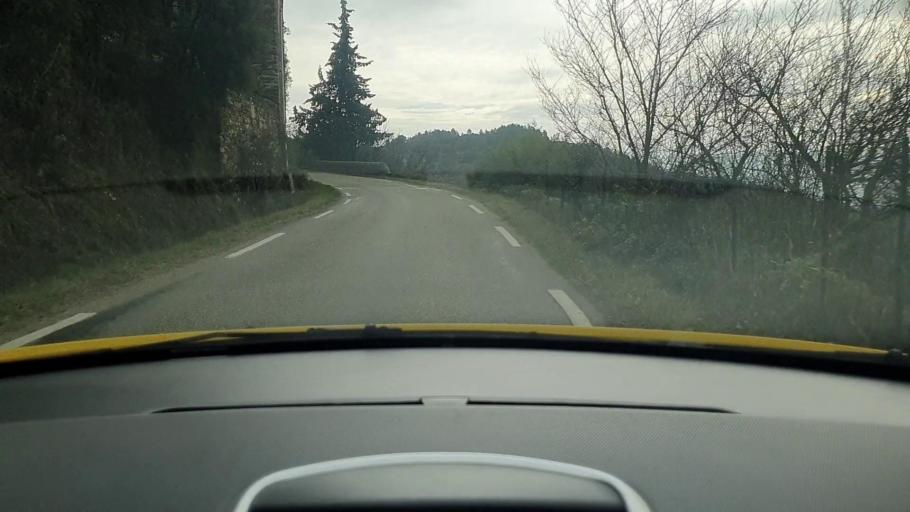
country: FR
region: Languedoc-Roussillon
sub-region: Departement du Gard
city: Besseges
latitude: 44.3391
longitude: 4.0498
